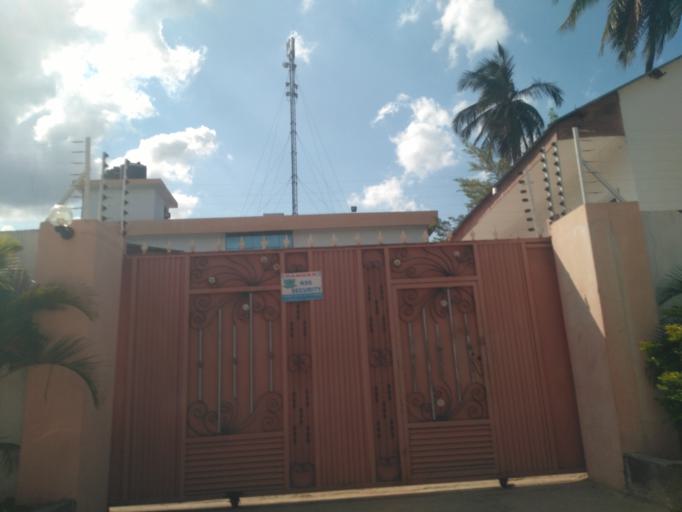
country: TZ
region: Dar es Salaam
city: Magomeni
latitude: -6.7746
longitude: 39.2574
